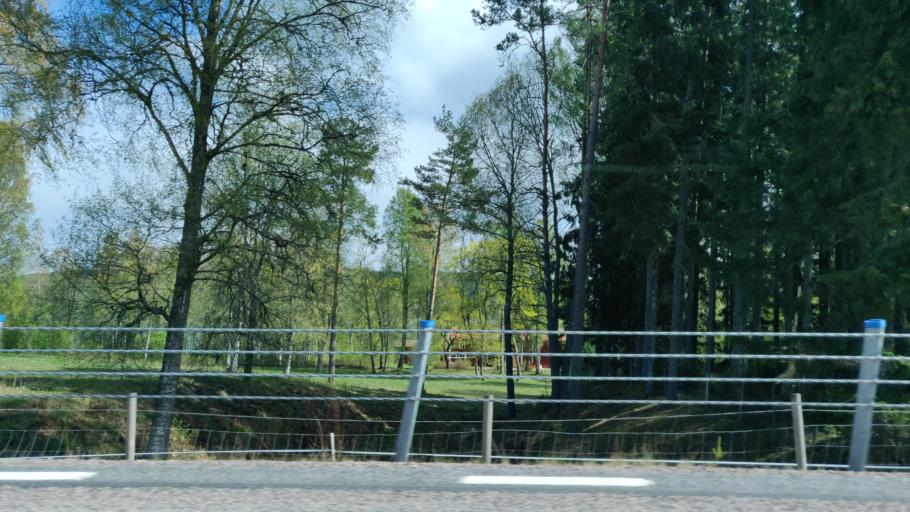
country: SE
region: Vaermland
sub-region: Munkfors Kommun
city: Munkfors
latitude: 59.8493
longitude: 13.7114
